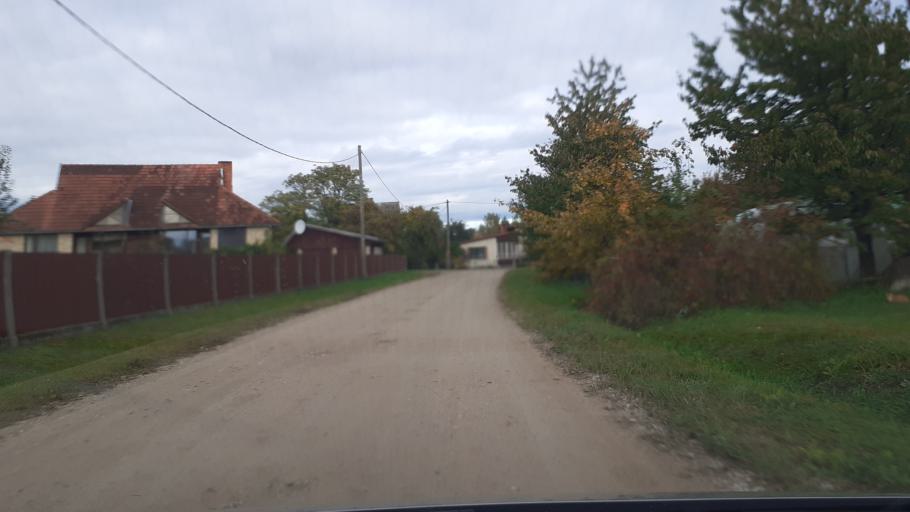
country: LV
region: Kuldigas Rajons
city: Kuldiga
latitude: 56.9658
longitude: 21.9926
